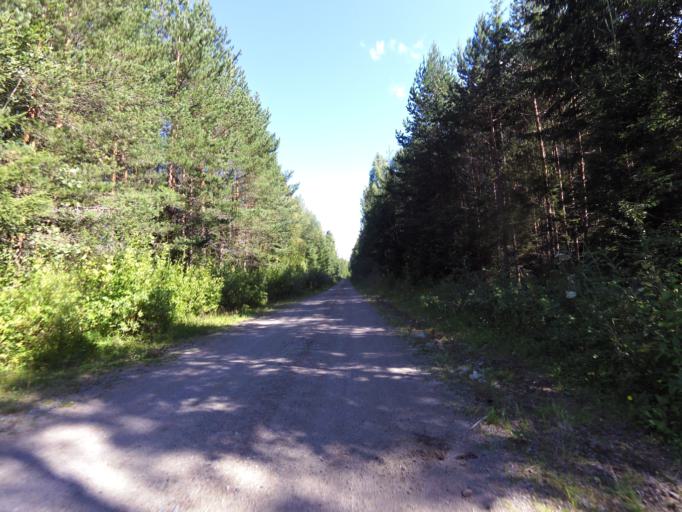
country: SE
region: Gaevleborg
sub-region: Hofors Kommun
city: Hofors
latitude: 60.5102
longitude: 16.3498
